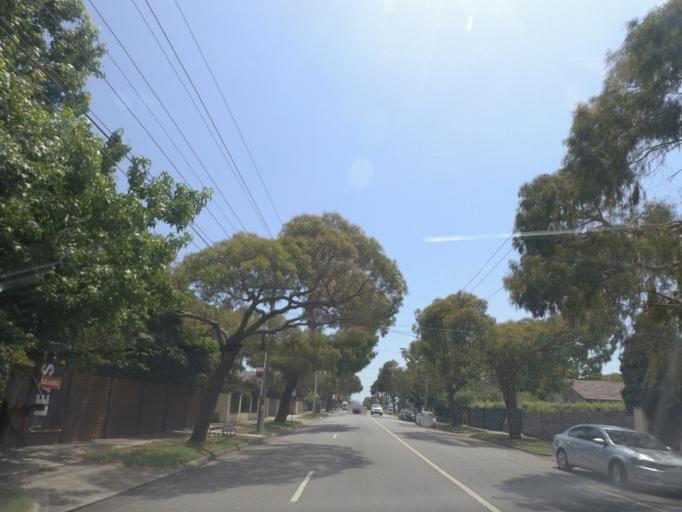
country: AU
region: Victoria
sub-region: Bayside
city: Black Rock
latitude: -37.9549
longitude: 145.0204
